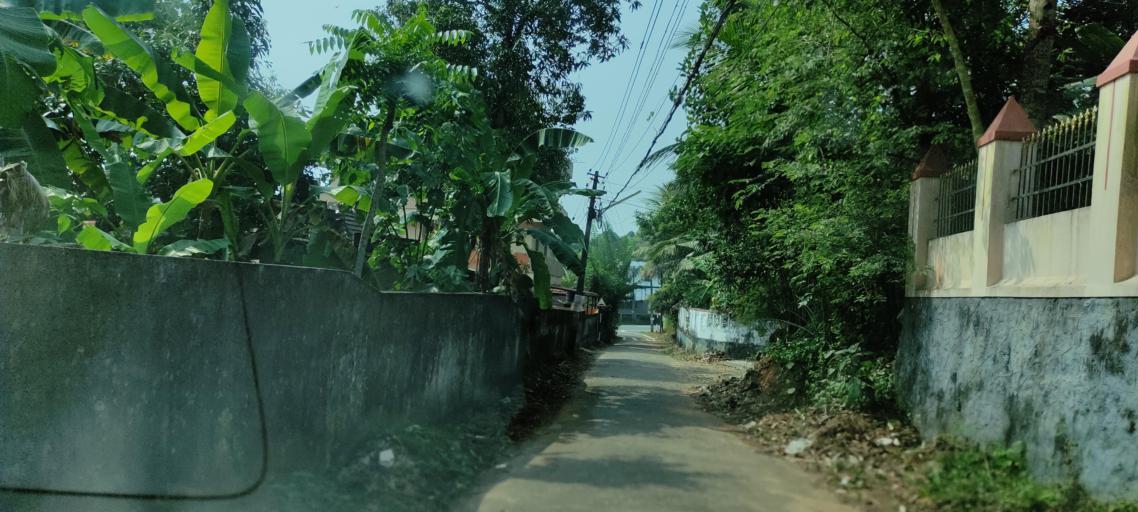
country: IN
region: Kerala
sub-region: Pattanamtitta
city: Adur
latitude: 9.2102
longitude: 76.6878
